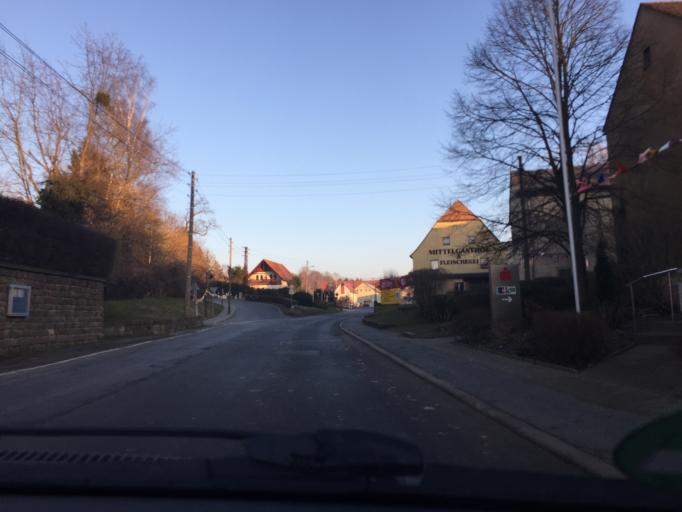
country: DE
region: Saxony
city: Struppen
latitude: 50.9357
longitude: 14.0084
